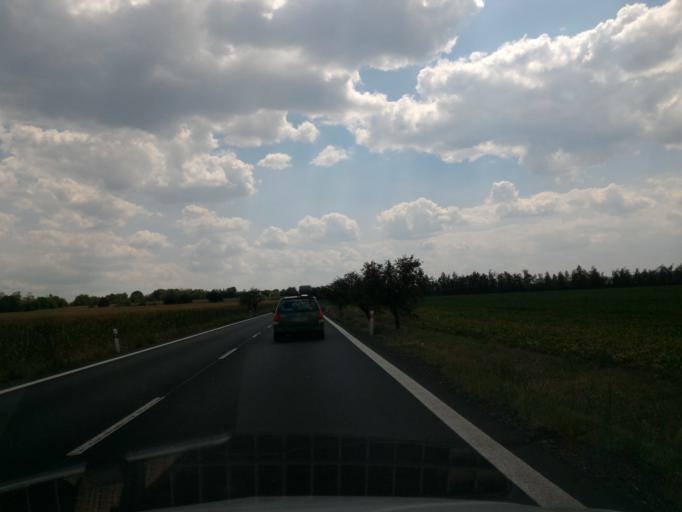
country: CZ
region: Central Bohemia
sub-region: Okres Kutna Hora
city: Caslav
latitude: 49.8787
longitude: 15.4282
